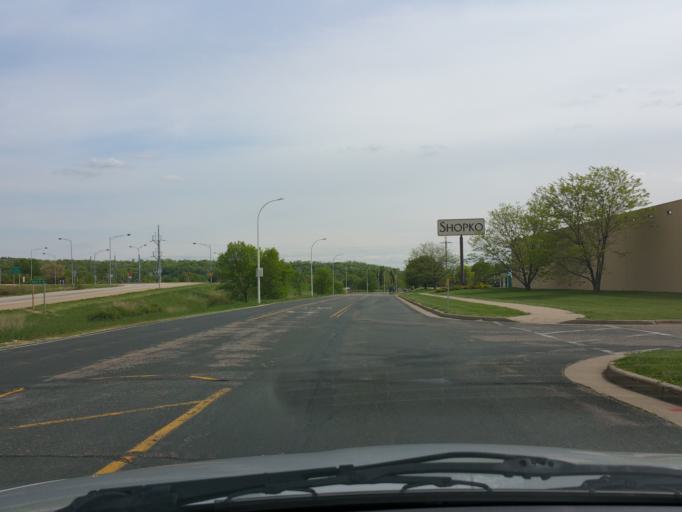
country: US
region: Wisconsin
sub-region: Pierce County
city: River Falls
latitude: 44.8799
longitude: -92.6243
